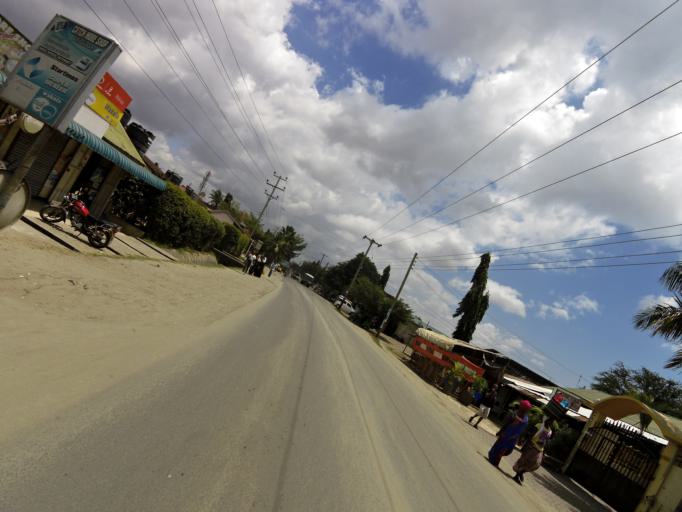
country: TZ
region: Dar es Salaam
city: Magomeni
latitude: -6.7881
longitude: 39.2293
